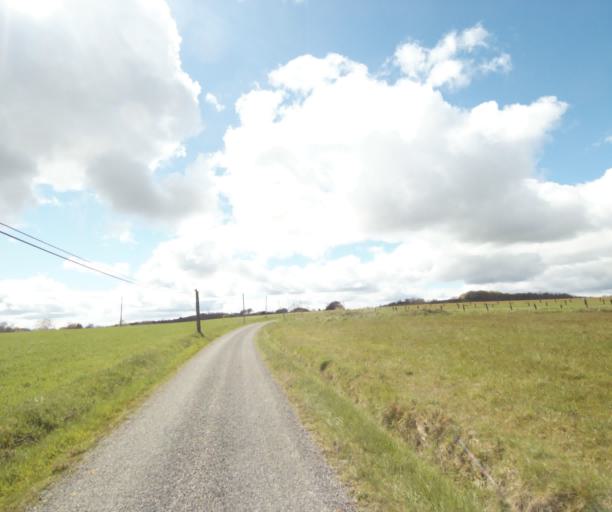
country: FR
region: Midi-Pyrenees
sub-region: Departement de l'Ariege
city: Saverdun
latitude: 43.1991
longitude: 1.5845
